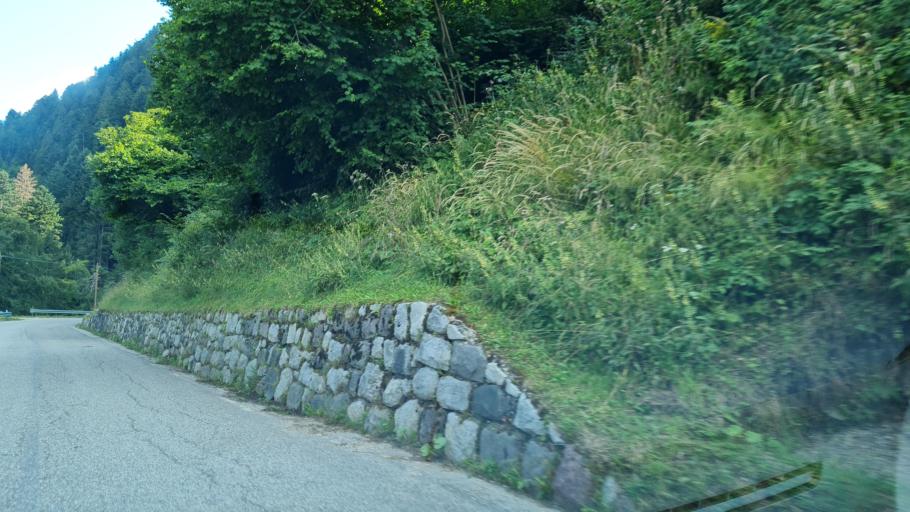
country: IT
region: Trentino-Alto Adige
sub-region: Provincia di Trento
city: Telve di Sopra
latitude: 46.1227
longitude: 11.4816
